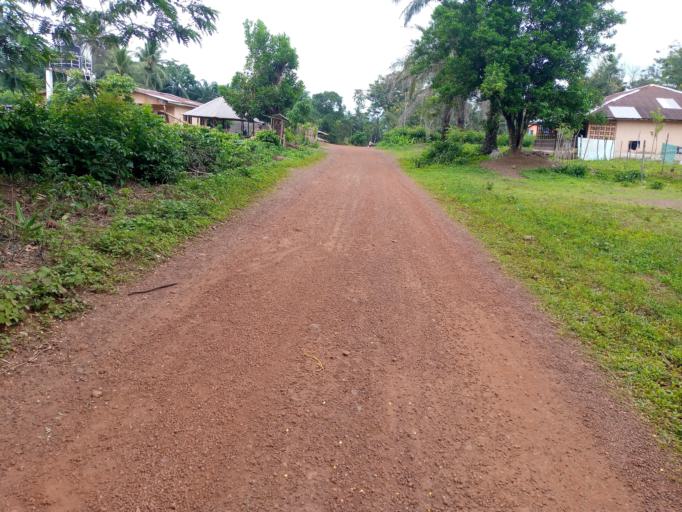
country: SL
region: Southern Province
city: Moyamba
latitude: 8.0518
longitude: -12.4628
